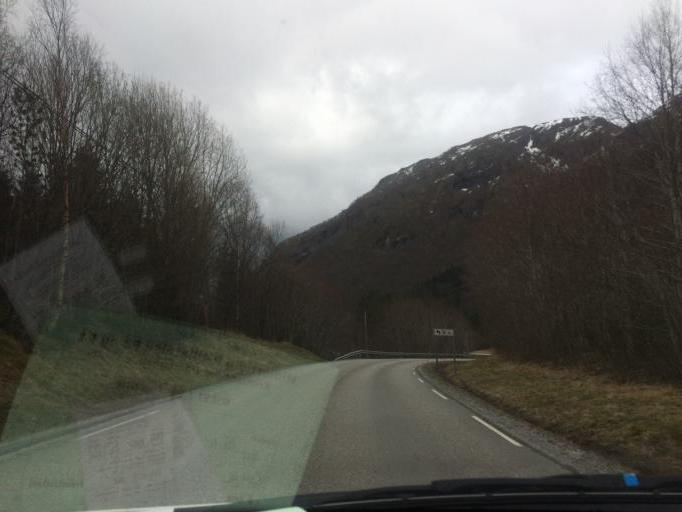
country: NO
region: More og Romsdal
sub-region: Gjemnes
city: Batnfjordsora
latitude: 62.9670
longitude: 7.7389
